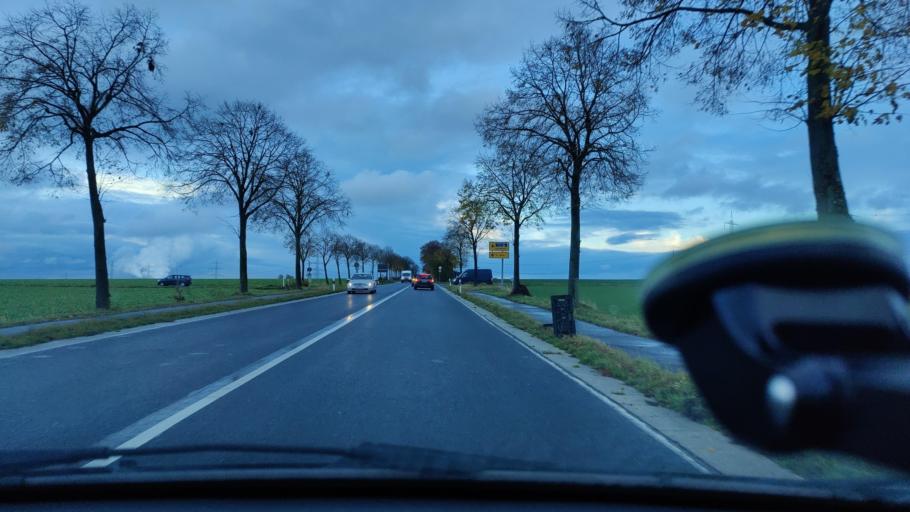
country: DE
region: North Rhine-Westphalia
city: Stolberg
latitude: 50.8228
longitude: 6.2086
